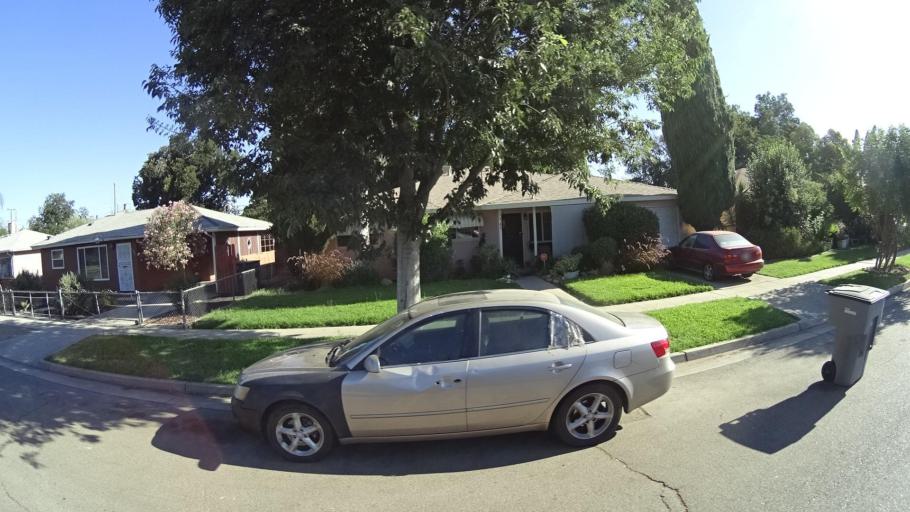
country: US
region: California
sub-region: Fresno County
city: Fresno
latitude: 36.7059
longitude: -119.7943
